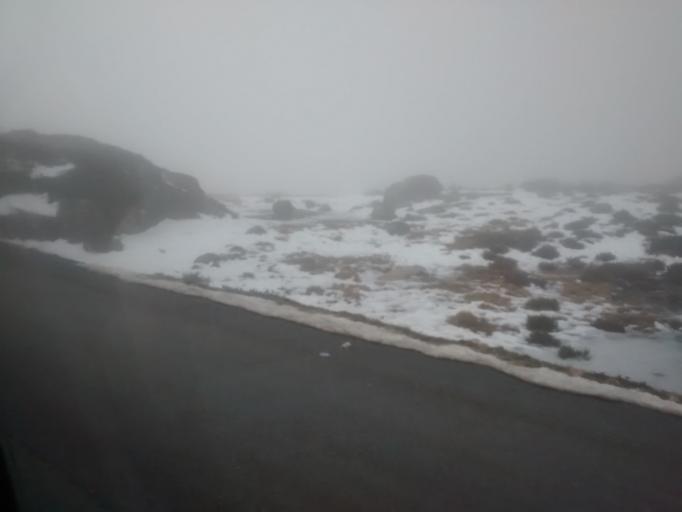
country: PT
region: Guarda
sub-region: Seia
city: Seia
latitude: 40.3597
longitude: -7.6542
